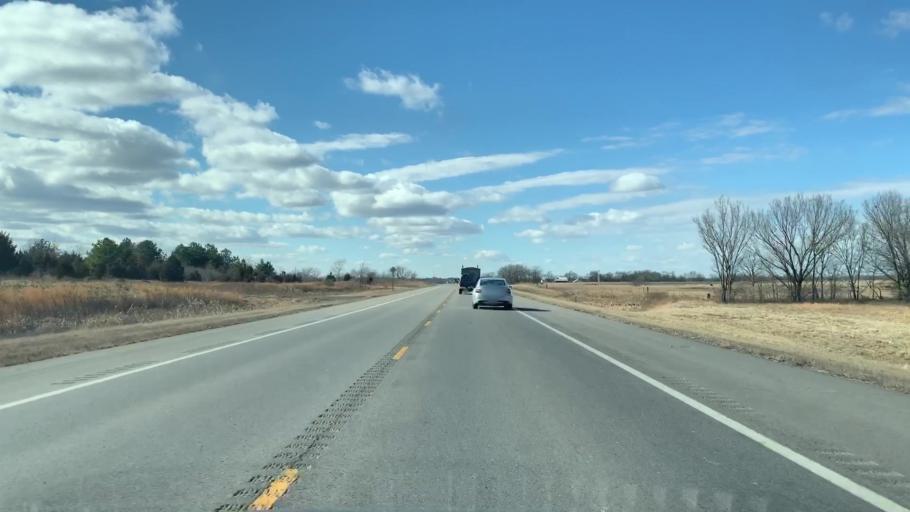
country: US
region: Kansas
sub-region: Crawford County
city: Pittsburg
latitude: 37.3396
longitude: -94.8447
